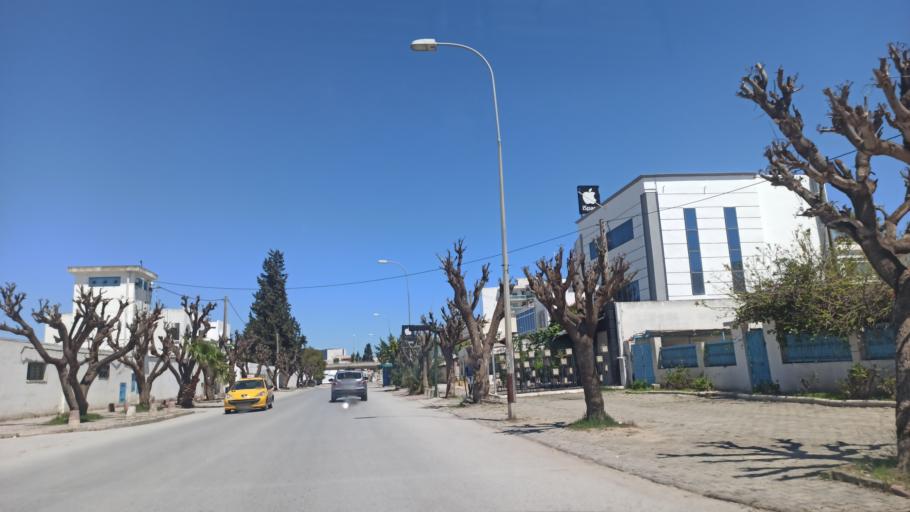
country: TN
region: Tunis
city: Tunis
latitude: 36.8290
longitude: 10.1855
